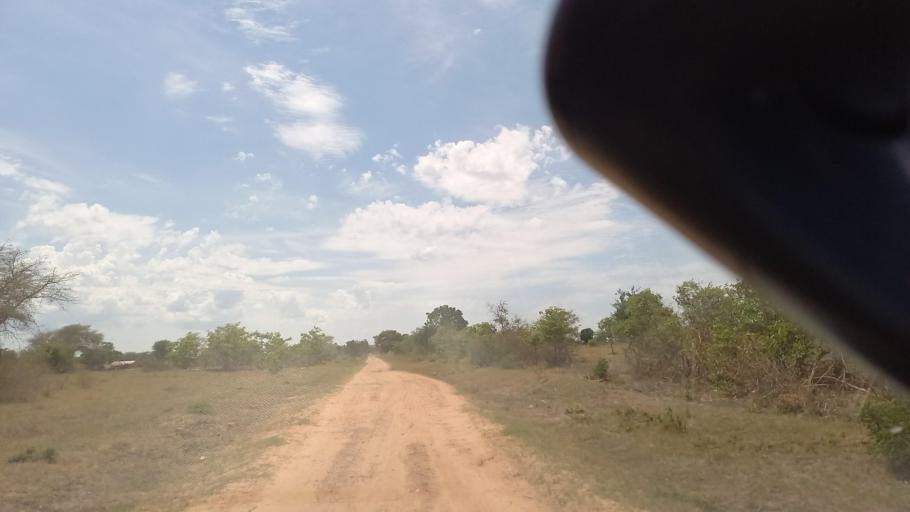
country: ZM
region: Southern
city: Mazabuka
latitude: -16.1432
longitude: 27.7690
